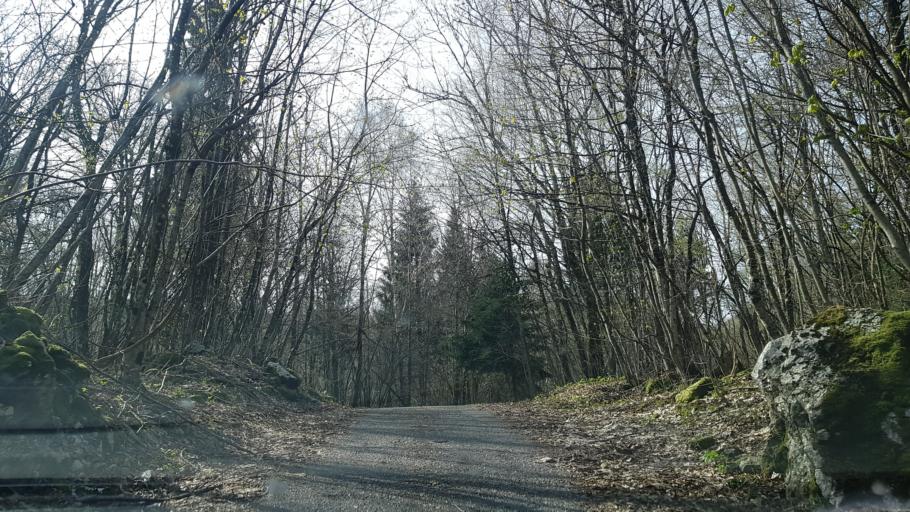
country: IT
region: Friuli Venezia Giulia
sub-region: Provincia di Udine
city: Trasaghis
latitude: 46.2860
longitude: 13.0154
